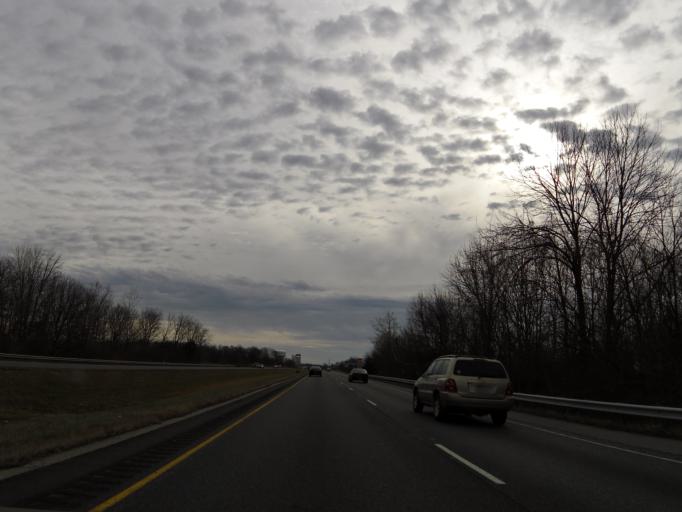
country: US
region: Indiana
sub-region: Hendricks County
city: Brownsburg
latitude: 39.8707
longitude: -86.4227
